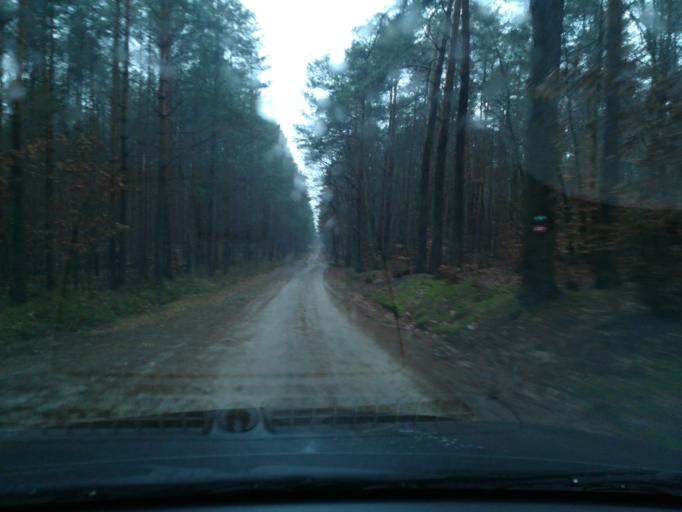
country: PL
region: Subcarpathian Voivodeship
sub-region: Powiat lancucki
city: Bialobrzegi
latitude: 50.1303
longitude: 22.3595
